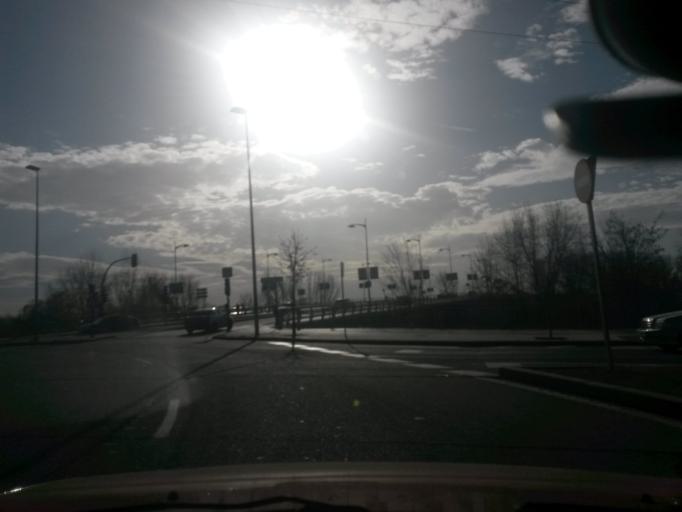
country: ES
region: Castille and Leon
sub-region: Provincia de Salamanca
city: Salamanca
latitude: 40.9612
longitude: -5.6450
